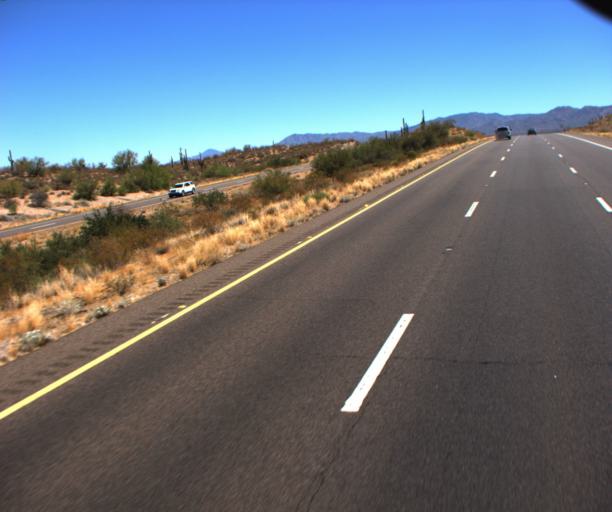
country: US
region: Arizona
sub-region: Maricopa County
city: Rio Verde
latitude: 33.6301
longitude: -111.5555
